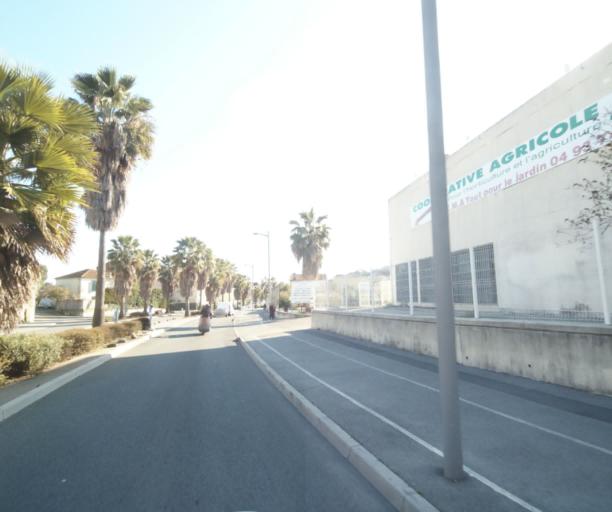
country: FR
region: Provence-Alpes-Cote d'Azur
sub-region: Departement des Alpes-Maritimes
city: Antibes
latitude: 43.5954
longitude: 7.1146
